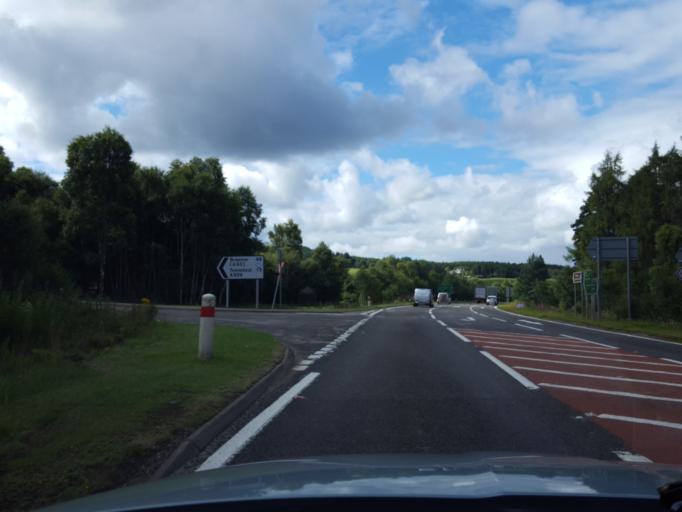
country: GB
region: Scotland
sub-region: Highland
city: Grantown on Spey
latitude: 57.3167
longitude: -3.5905
